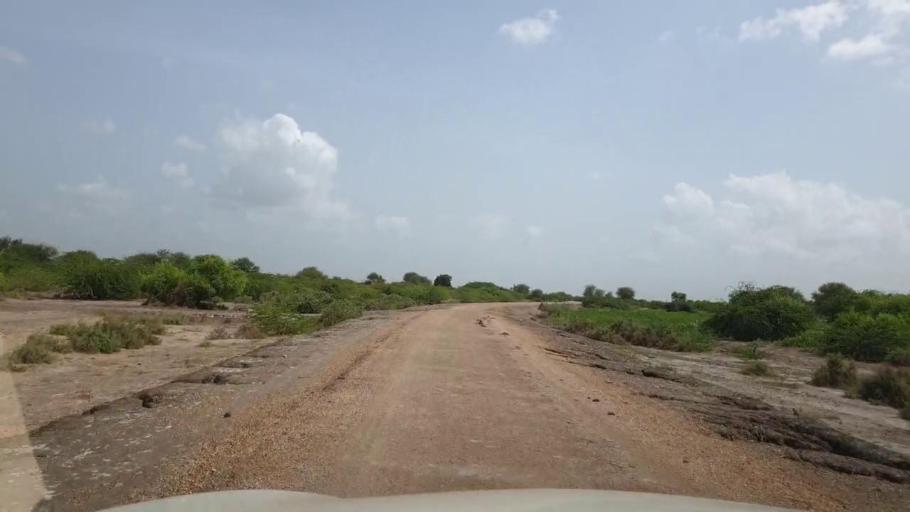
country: PK
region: Sindh
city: Kadhan
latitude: 24.3935
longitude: 68.7949
